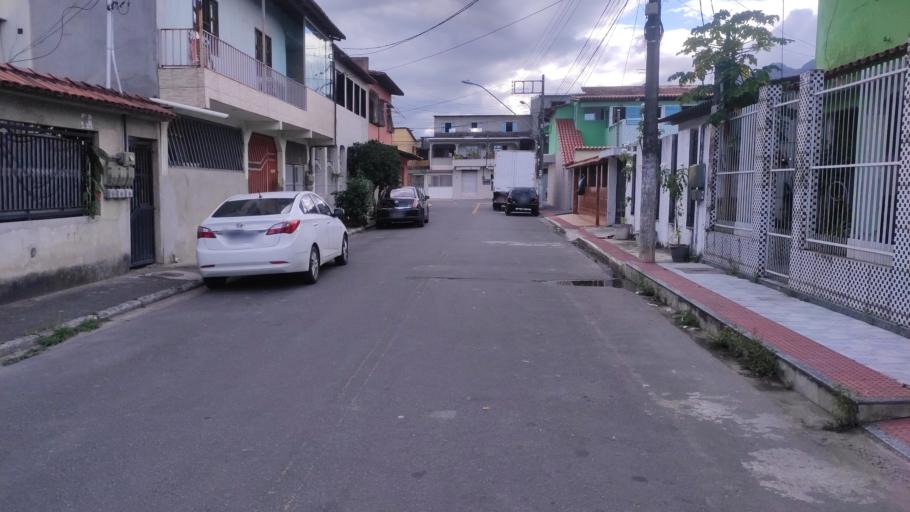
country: BR
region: Espirito Santo
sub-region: Serra
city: Serra
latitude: -20.1944
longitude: -40.2726
